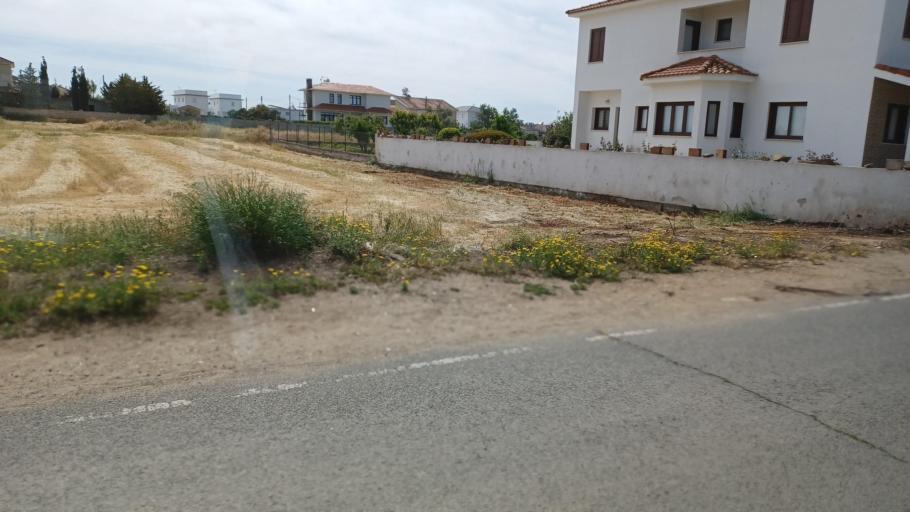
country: CY
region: Lefkosia
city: Kokkinotrimithia
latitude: 35.1519
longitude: 33.2065
